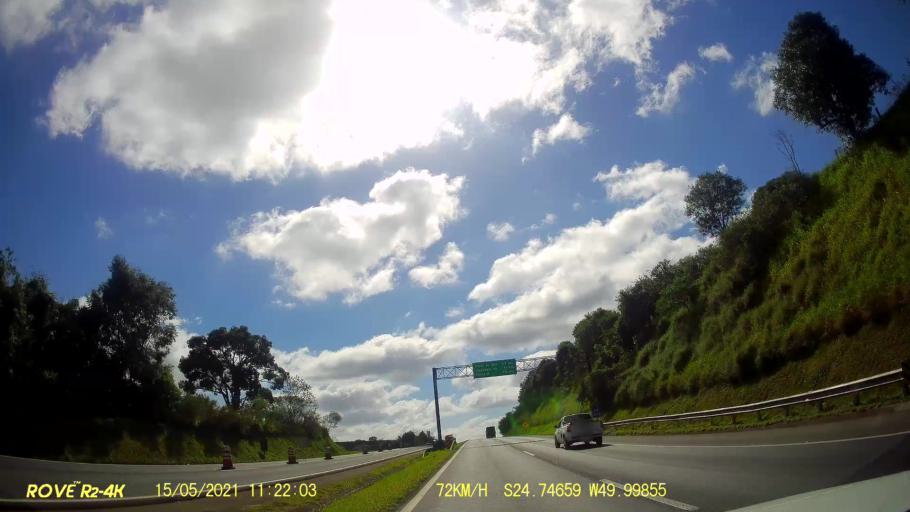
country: BR
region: Parana
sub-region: Castro
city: Castro
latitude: -24.7467
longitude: -49.9986
